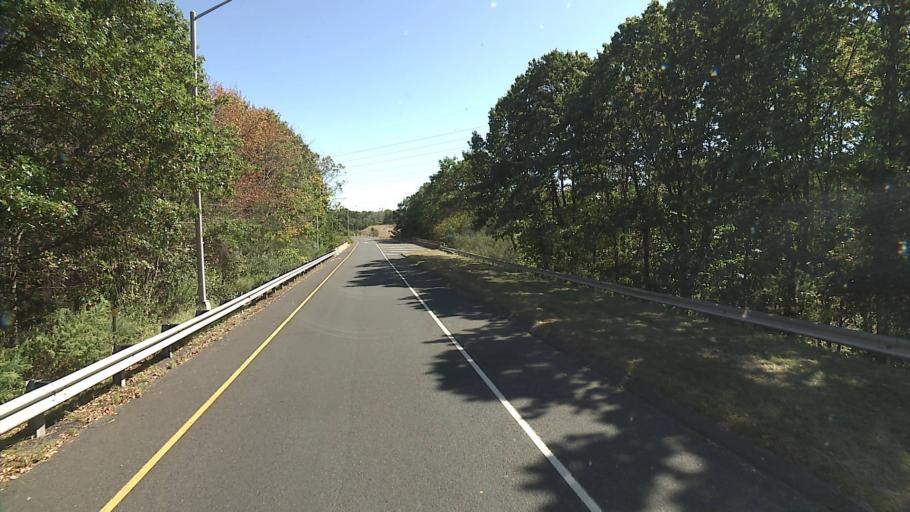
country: US
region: Connecticut
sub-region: New Haven County
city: Cheshire Village
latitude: 41.5748
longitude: -72.8991
